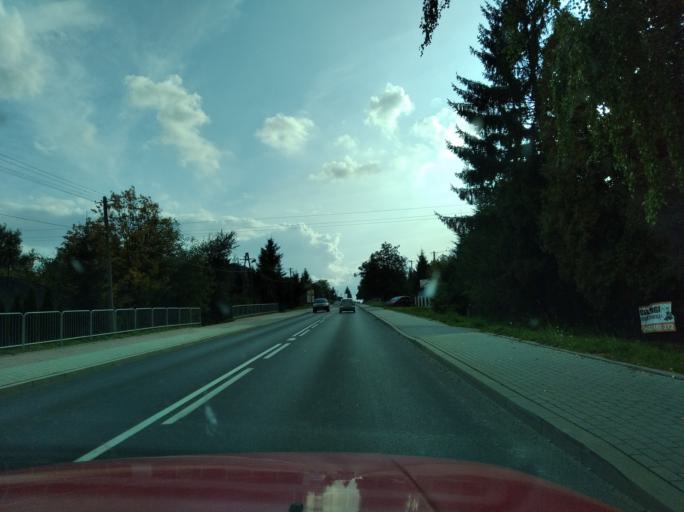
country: PL
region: Subcarpathian Voivodeship
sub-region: Powiat jaroslawski
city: Jaroslaw
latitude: 49.9997
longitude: 22.6707
